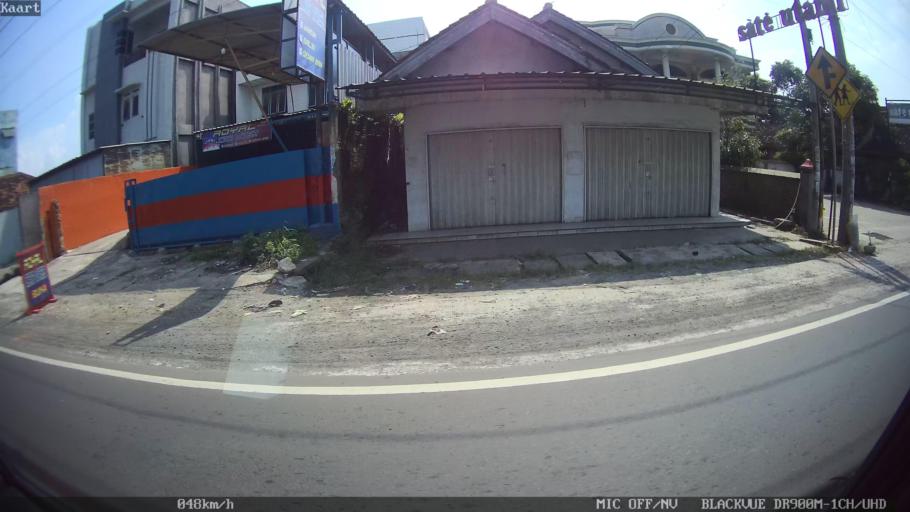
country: ID
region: Lampung
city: Natar
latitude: -5.3142
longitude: 105.1956
